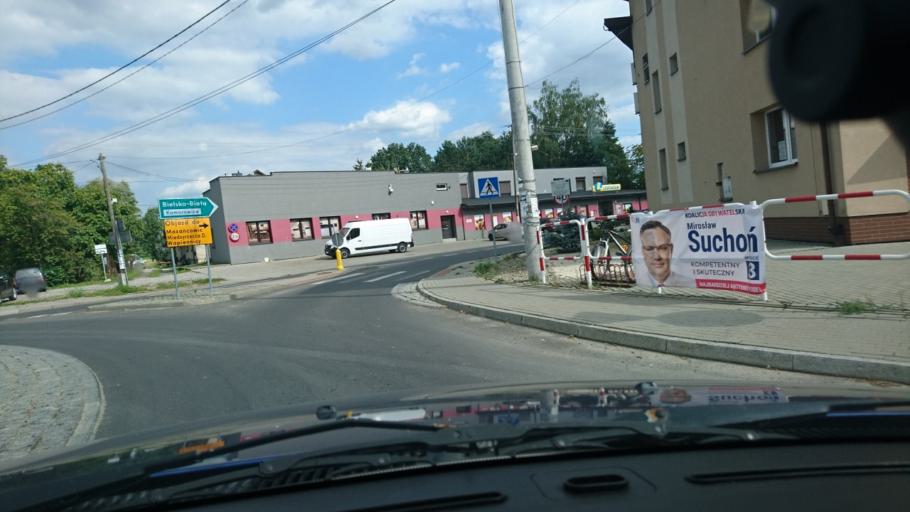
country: PL
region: Silesian Voivodeship
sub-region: Powiat bielski
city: Ligota
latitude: 49.8803
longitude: 18.9482
